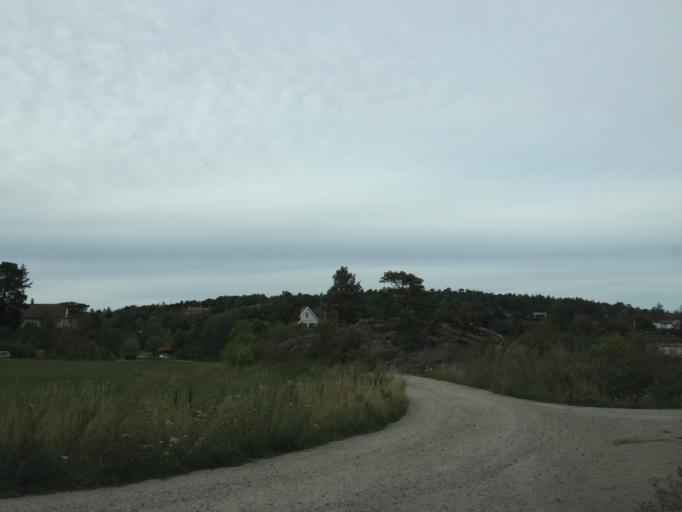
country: NO
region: Ostfold
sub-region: Hvaler
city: Skjaerhalden
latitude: 59.0357
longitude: 11.0537
